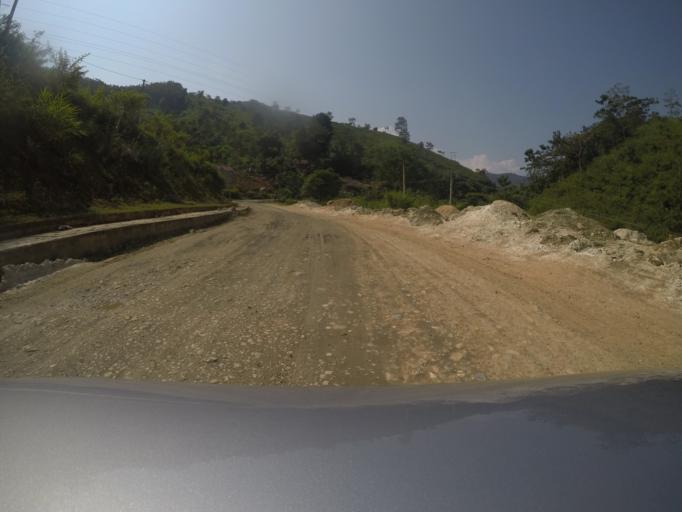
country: VN
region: Lao Cai
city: Thi Tran Khanh Yen
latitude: 22.1503
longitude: 104.3404
